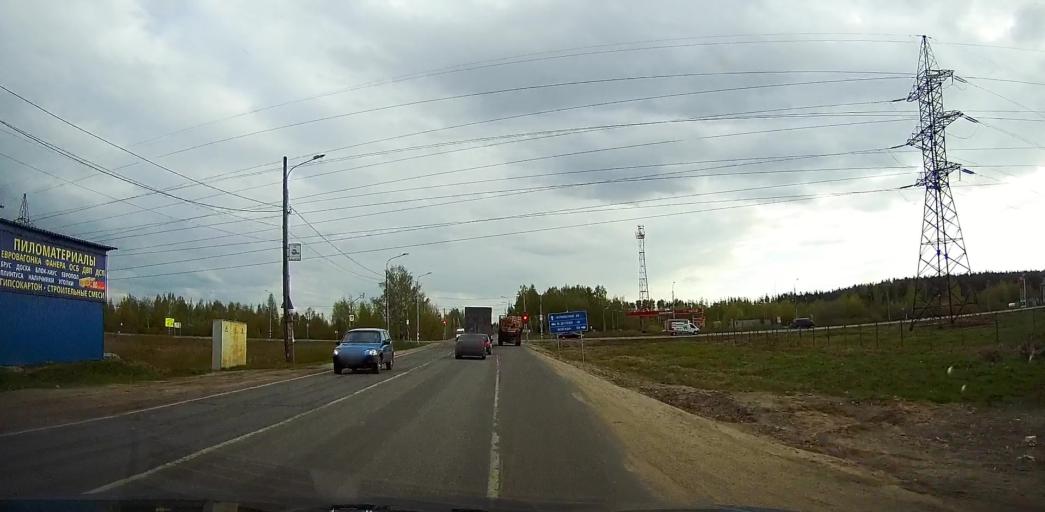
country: RU
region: Moskovskaya
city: Pavlovskiy Posad
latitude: 55.7493
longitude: 38.7036
